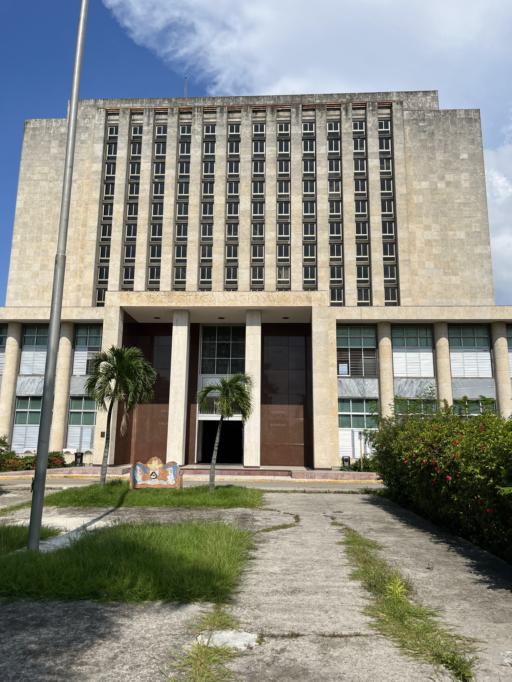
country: CU
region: La Habana
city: Havana
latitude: 23.1240
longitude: -82.3840
